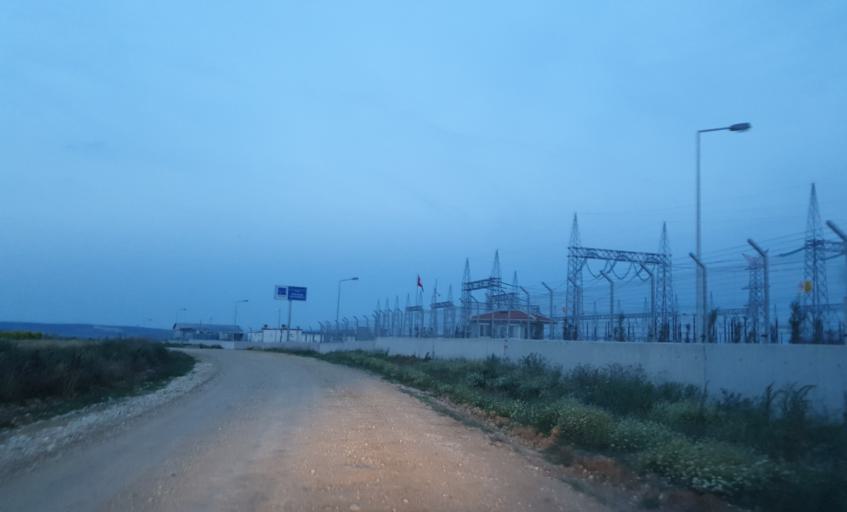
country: TR
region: Kirklareli
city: Vize
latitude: 41.5174
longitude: 27.7577
